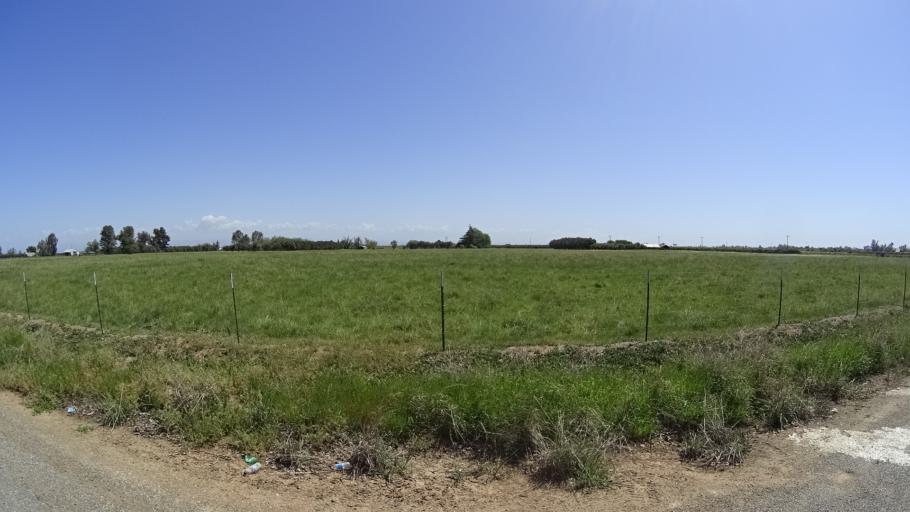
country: US
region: California
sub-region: Glenn County
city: Orland
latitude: 39.7809
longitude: -122.1836
